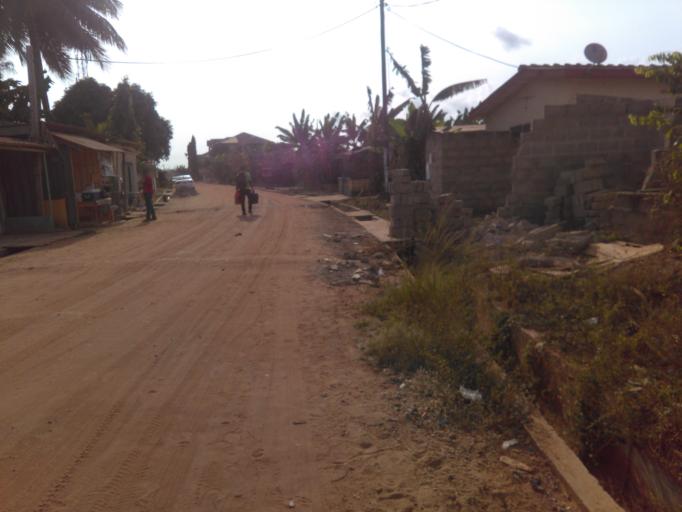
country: GH
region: Central
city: Cape Coast
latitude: 5.1103
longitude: -1.2945
